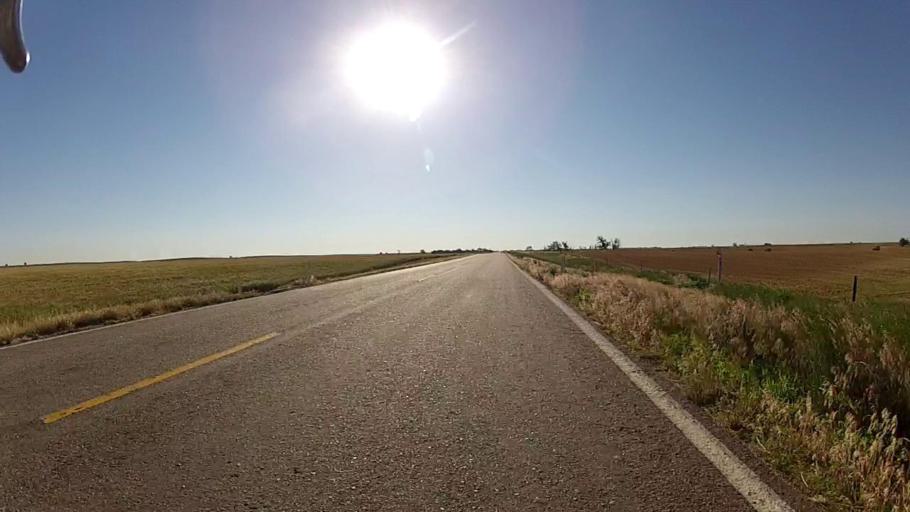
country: US
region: Kansas
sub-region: Ford County
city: Dodge City
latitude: 37.6458
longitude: -99.8082
